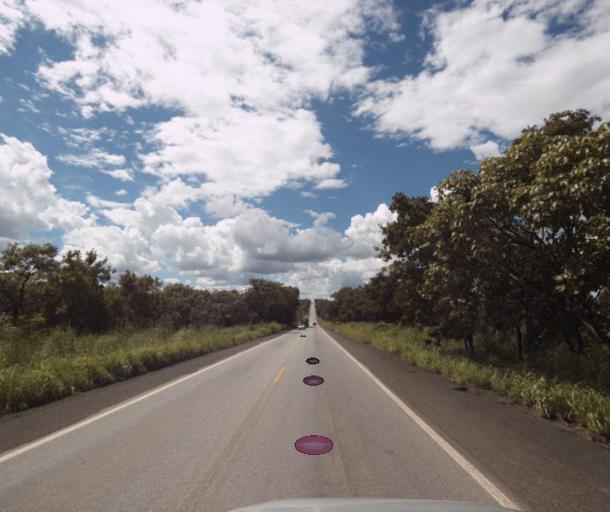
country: BR
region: Goias
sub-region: Porangatu
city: Porangatu
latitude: -13.8530
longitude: -49.0485
